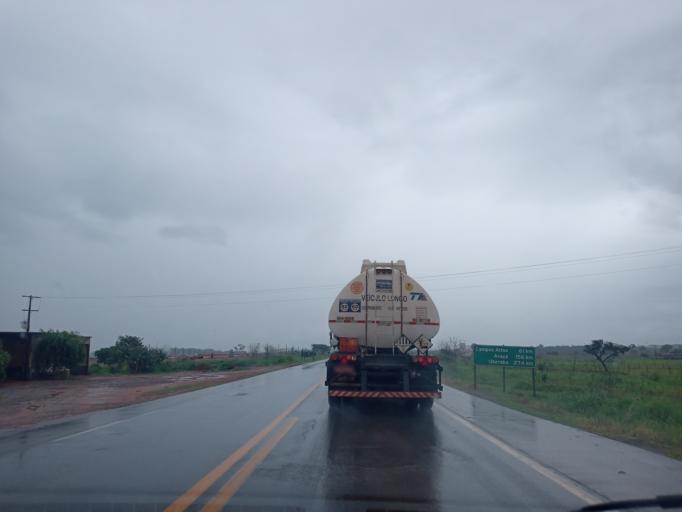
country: BR
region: Minas Gerais
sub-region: Luz
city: Luz
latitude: -19.7831
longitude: -45.6877
